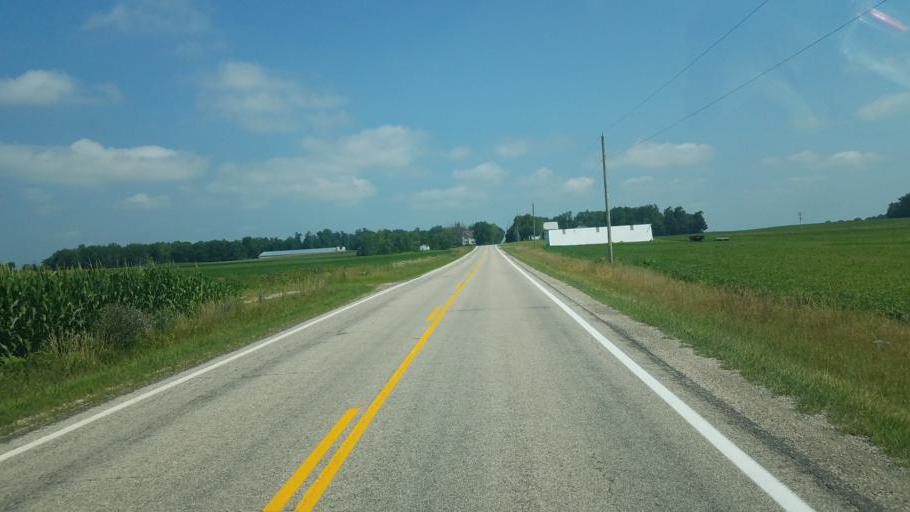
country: US
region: Ohio
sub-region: Crawford County
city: Bucyrus
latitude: 40.8544
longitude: -82.8556
